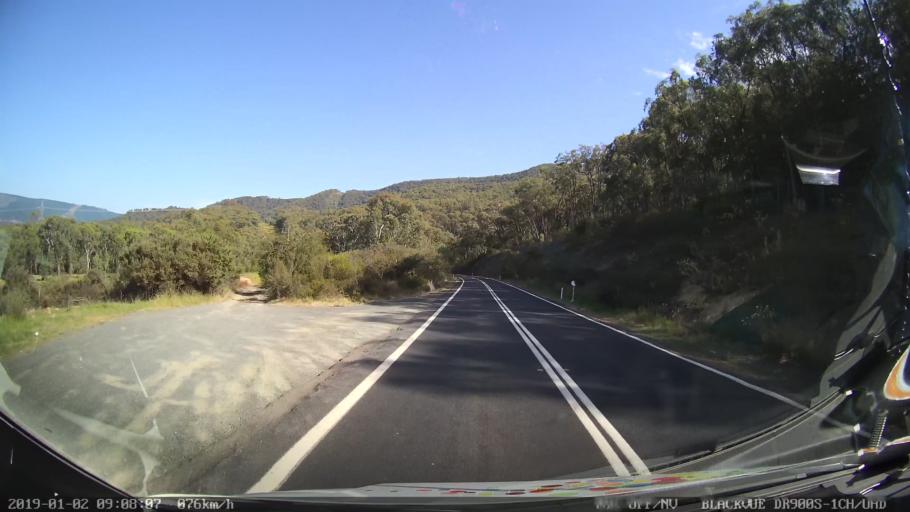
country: AU
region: New South Wales
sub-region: Tumut Shire
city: Tumut
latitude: -35.5335
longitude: 148.2946
